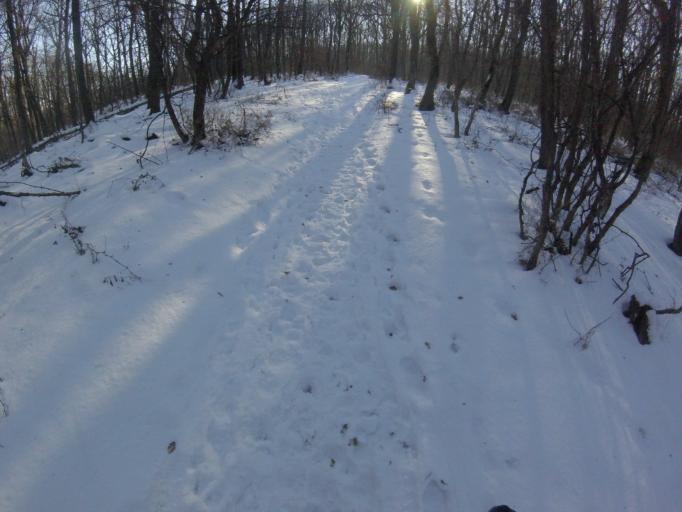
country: SK
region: Nitriansky
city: Sahy
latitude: 47.9884
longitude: 18.8887
